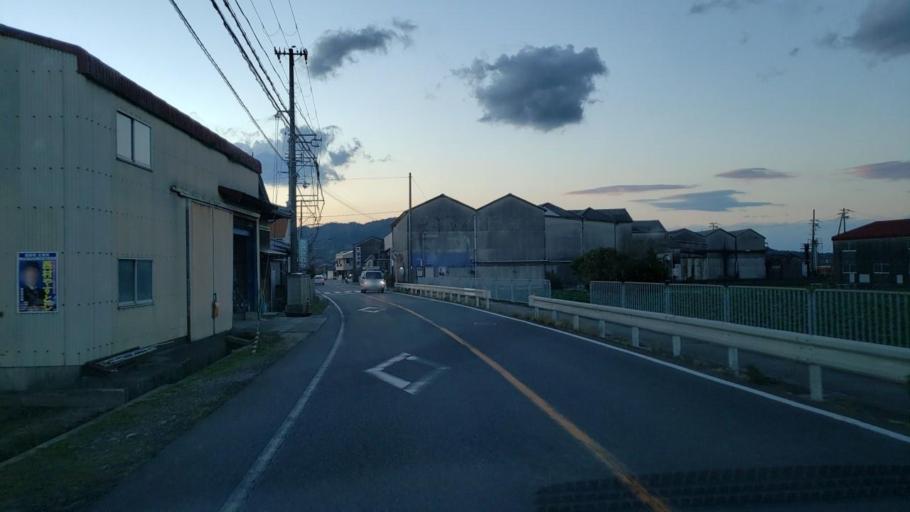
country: JP
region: Hyogo
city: Fukura
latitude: 34.3003
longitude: 134.7582
